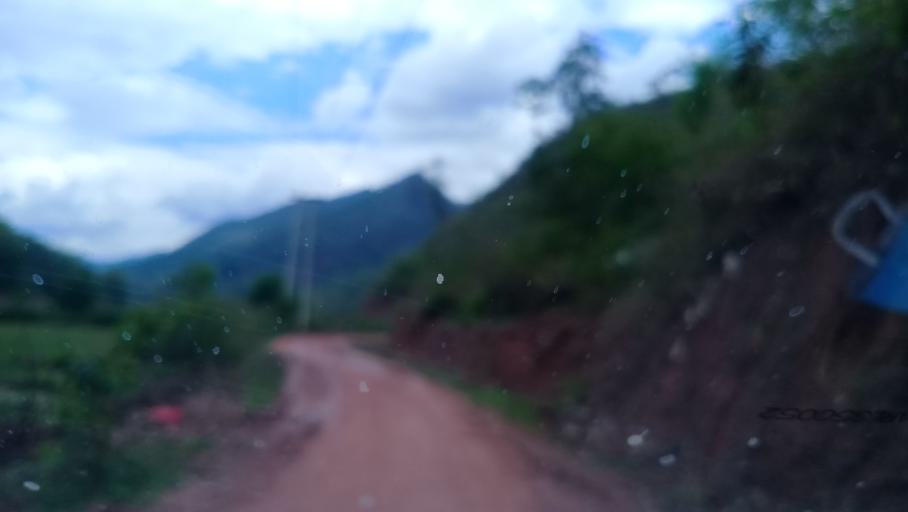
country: CN
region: Yunnan
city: Menglie
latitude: 22.1750
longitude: 101.7445
